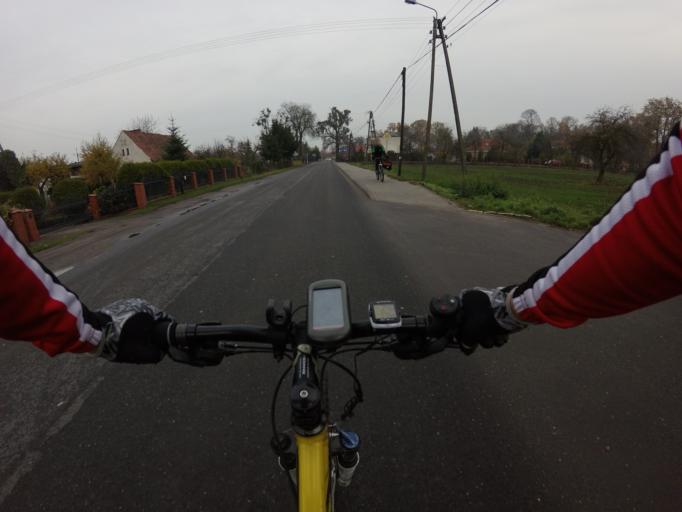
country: PL
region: Kujawsko-Pomorskie
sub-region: Powiat bydgoski
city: Osielsko
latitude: 53.2158
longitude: 18.0560
